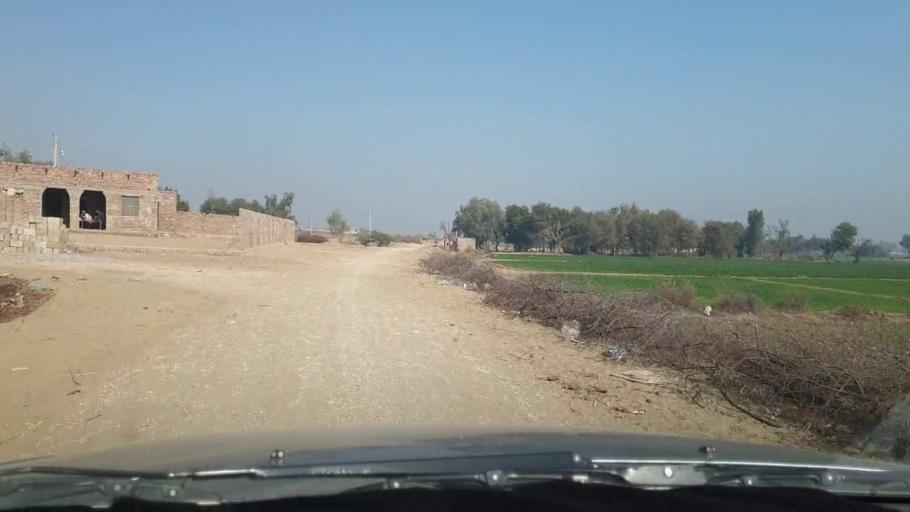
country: PK
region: Sindh
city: Khanpur
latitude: 27.8093
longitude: 69.5625
